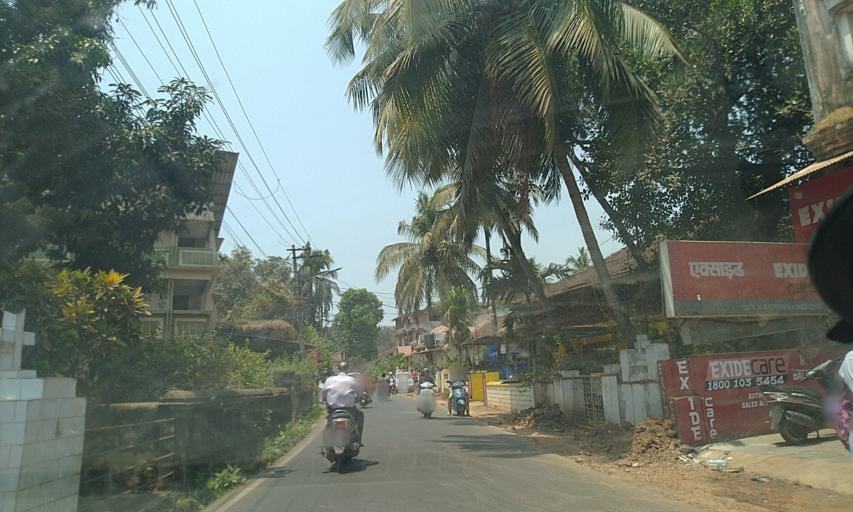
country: IN
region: Goa
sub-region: North Goa
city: Mapuca
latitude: 15.5932
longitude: 73.8052
